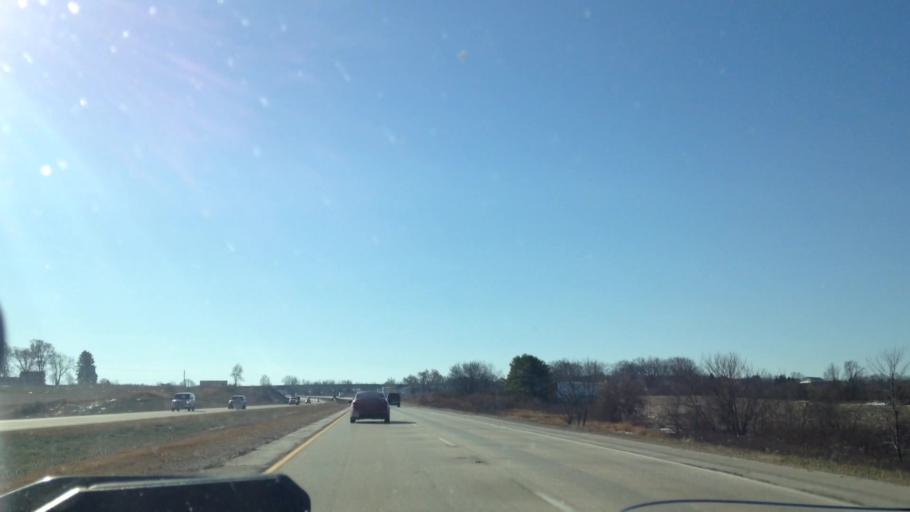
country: US
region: Wisconsin
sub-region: Washington County
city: Jackson
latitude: 43.3001
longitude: -88.1870
